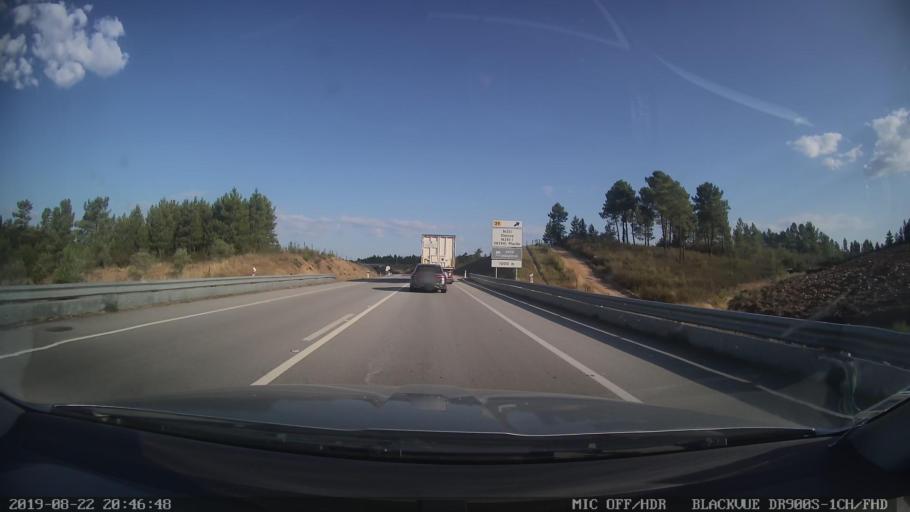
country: PT
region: Castelo Branco
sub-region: Proenca-A-Nova
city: Proenca-a-Nova
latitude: 39.7296
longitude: -7.8796
